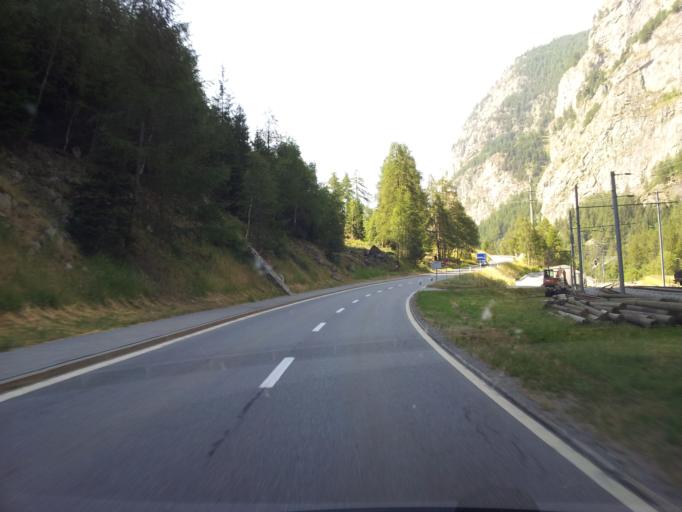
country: CH
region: Valais
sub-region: Visp District
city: Sankt Niklaus
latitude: 46.1432
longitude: 7.7930
